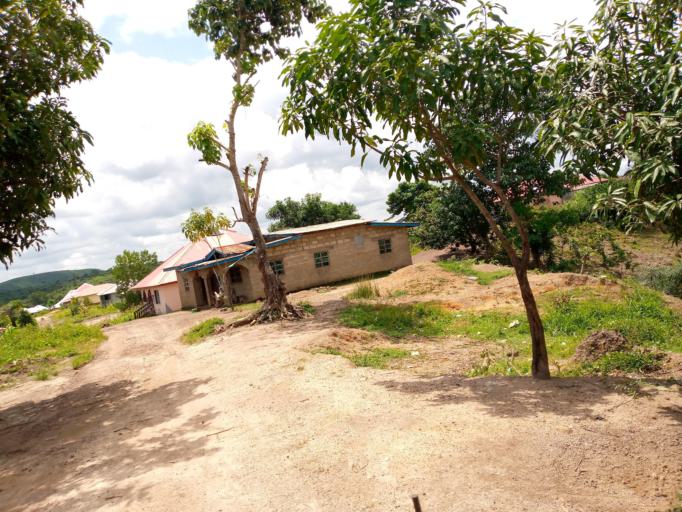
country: SL
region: Northern Province
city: Magburaka
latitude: 8.7306
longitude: -11.9386
